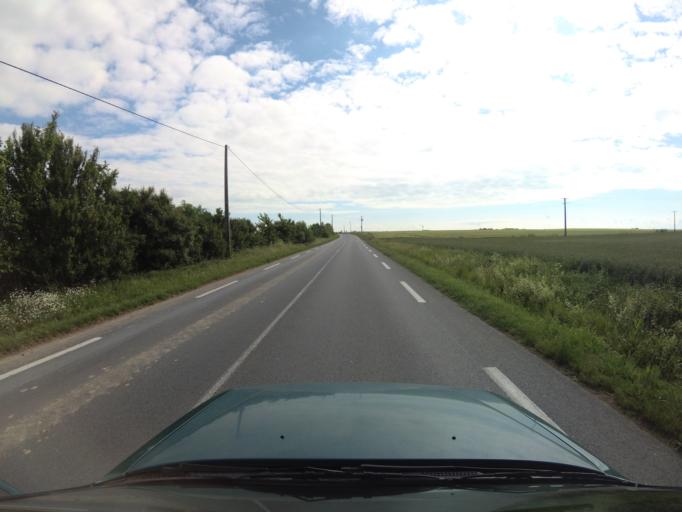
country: FR
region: Poitou-Charentes
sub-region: Departement de la Charente-Maritime
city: Saint-Xandre
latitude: 46.2258
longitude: -1.0827
